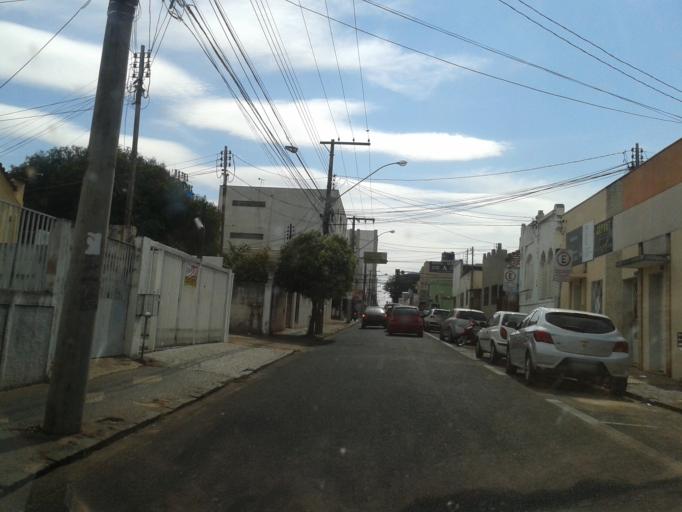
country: BR
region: Minas Gerais
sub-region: Uberlandia
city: Uberlandia
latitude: -18.9181
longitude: -48.2728
